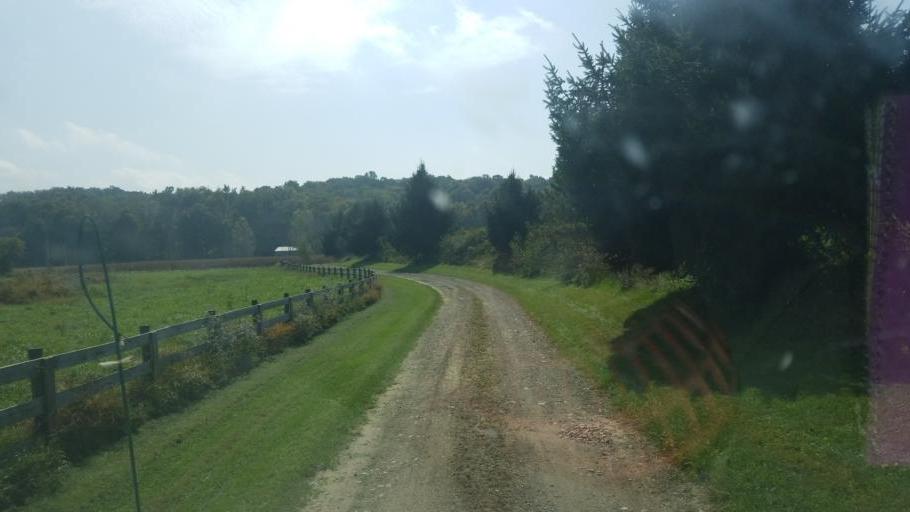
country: US
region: Ohio
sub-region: Sandusky County
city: Bellville
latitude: 40.5577
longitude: -82.4987
